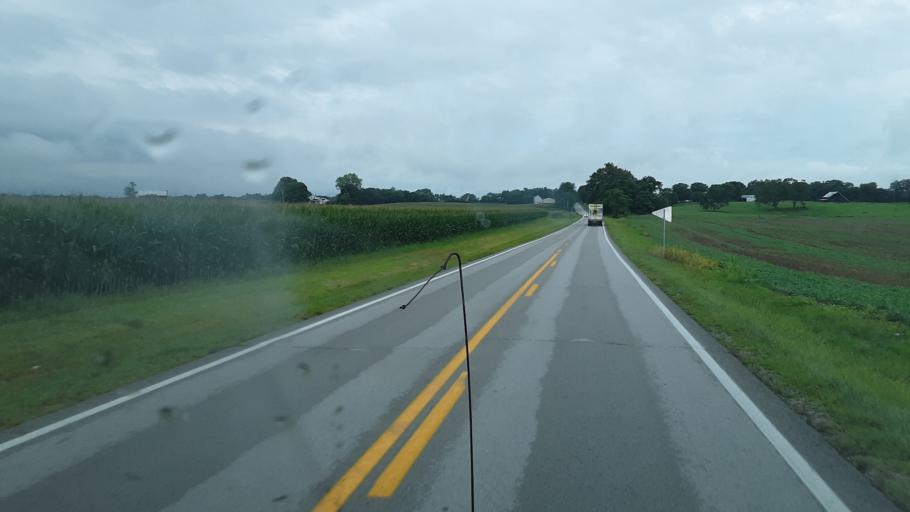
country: US
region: Kentucky
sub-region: Todd County
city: Elkton
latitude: 36.7573
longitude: -87.0338
